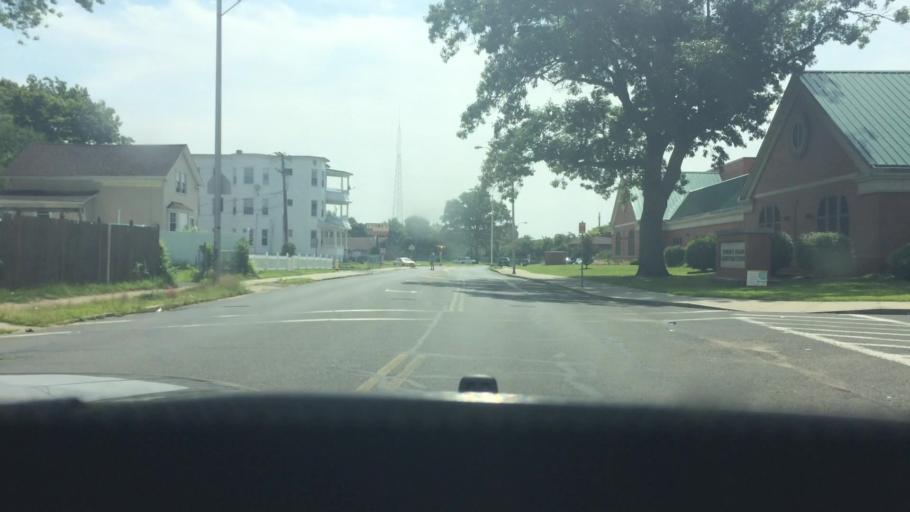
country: US
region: Massachusetts
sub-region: Hampden County
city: Springfield
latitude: 42.1209
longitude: -72.5870
